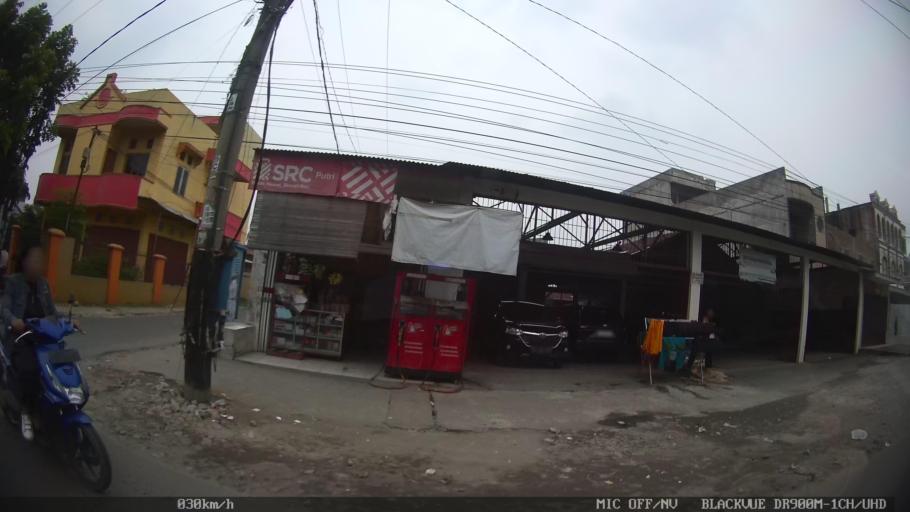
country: ID
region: North Sumatra
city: Medan
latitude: 3.5748
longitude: 98.7261
